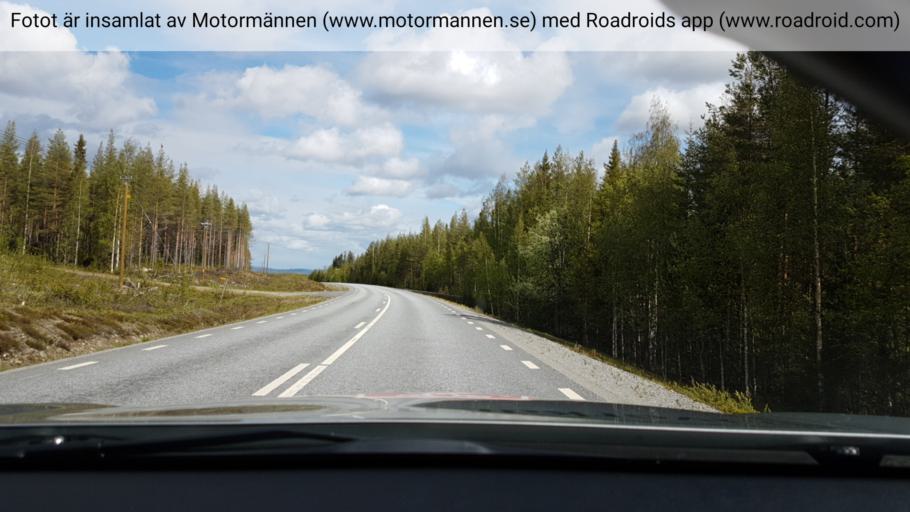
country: SE
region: Vaesterbotten
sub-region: Asele Kommun
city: Insjon
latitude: 64.1480
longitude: 17.9092
